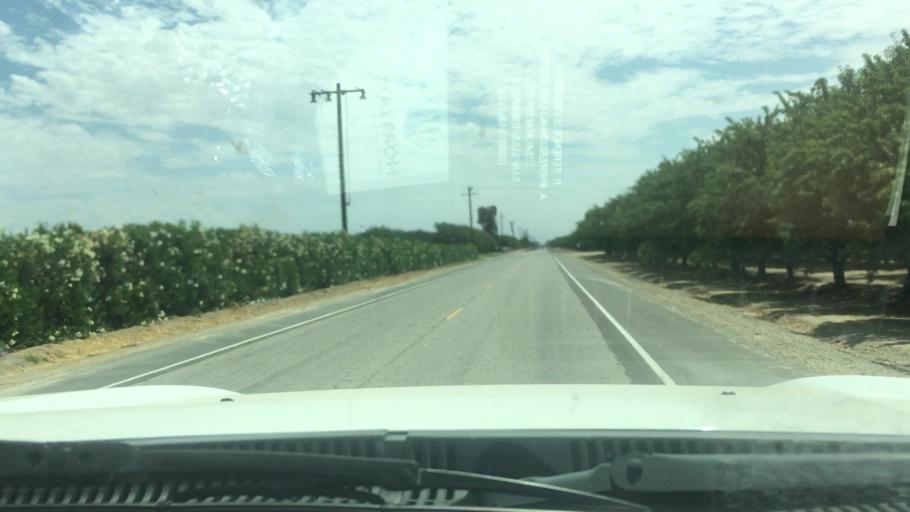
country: US
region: California
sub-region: Kern County
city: Wasco
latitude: 35.5579
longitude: -119.3690
